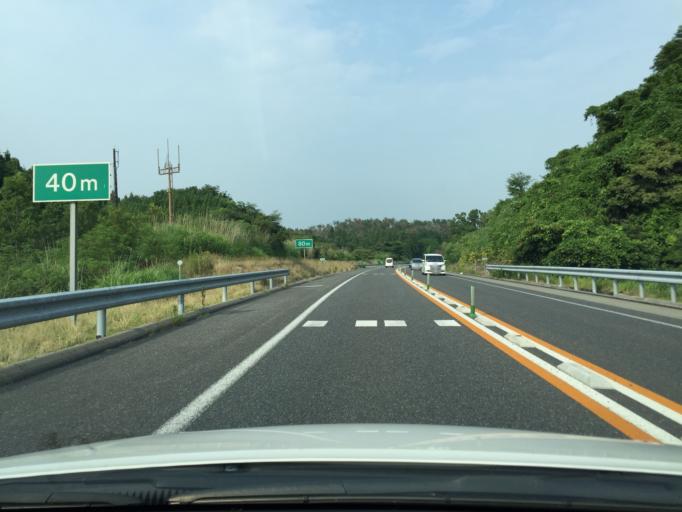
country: JP
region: Fukushima
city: Iwaki
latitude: 37.1199
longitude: 140.9193
